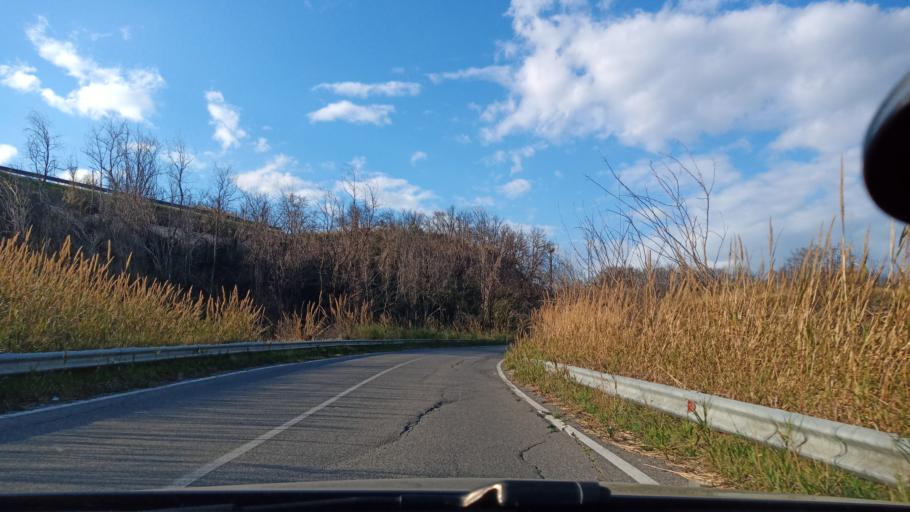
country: IT
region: Latium
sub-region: Citta metropolitana di Roma Capitale
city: Nazzano
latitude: 42.2045
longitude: 12.6045
